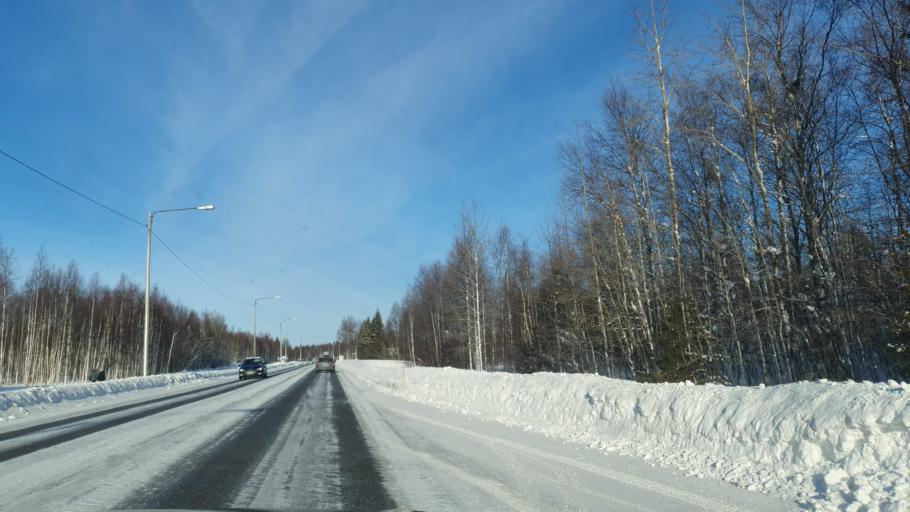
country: FI
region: Lapland
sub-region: Kemi-Tornio
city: Tornio
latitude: 65.8841
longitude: 24.1527
